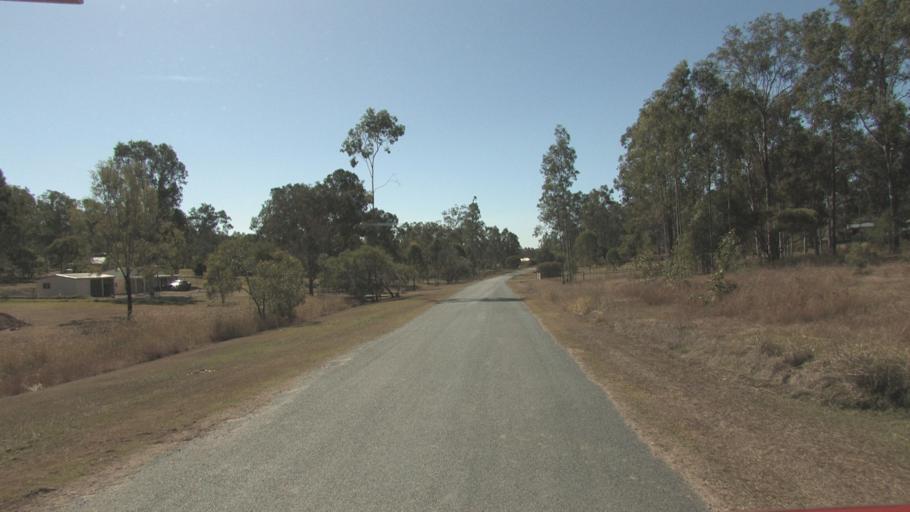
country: AU
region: Queensland
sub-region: Logan
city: Cedar Vale
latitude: -27.8614
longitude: 153.0325
